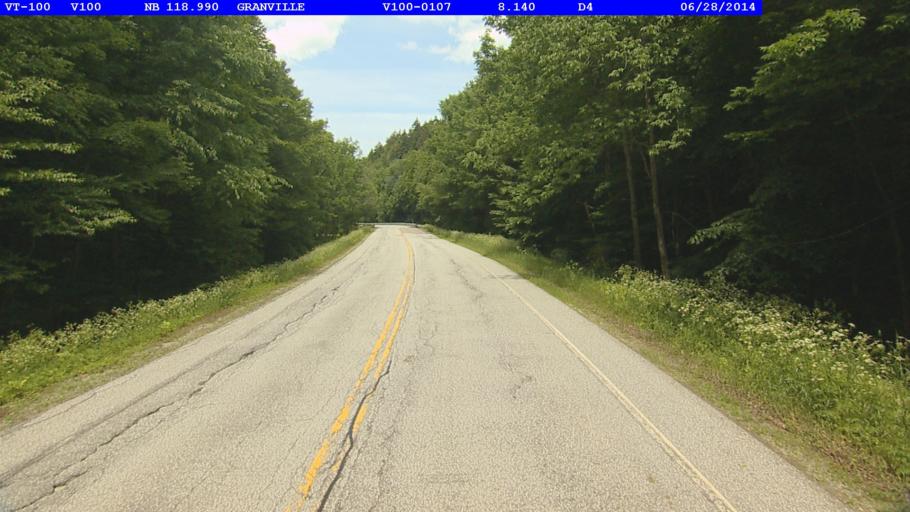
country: US
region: Vermont
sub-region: Washington County
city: Northfield
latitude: 44.0474
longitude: -72.8298
